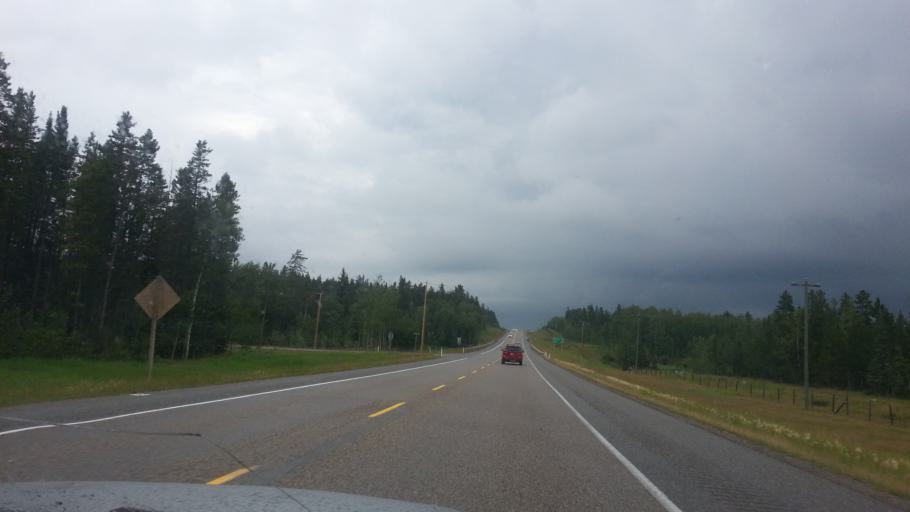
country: CA
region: Alberta
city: Cochrane
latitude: 50.9256
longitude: -114.5602
